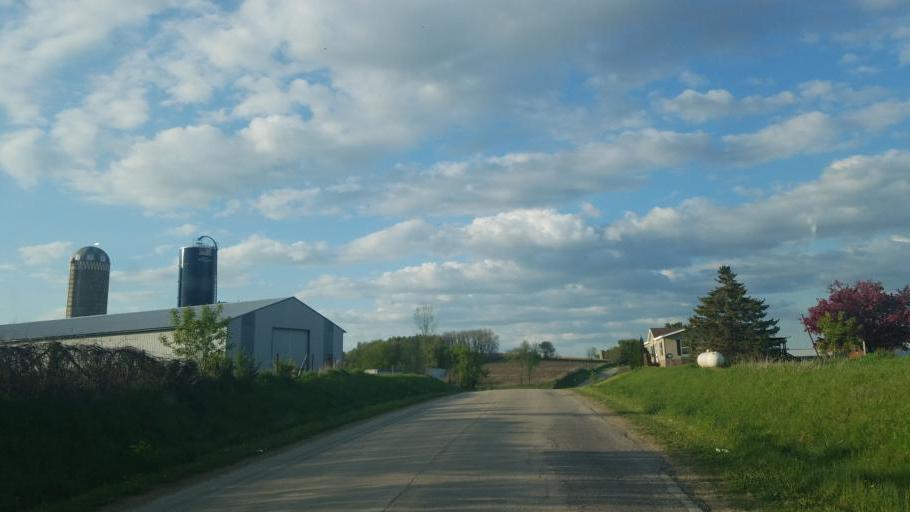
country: US
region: Wisconsin
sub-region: Vernon County
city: Hillsboro
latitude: 43.6623
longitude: -90.3299
